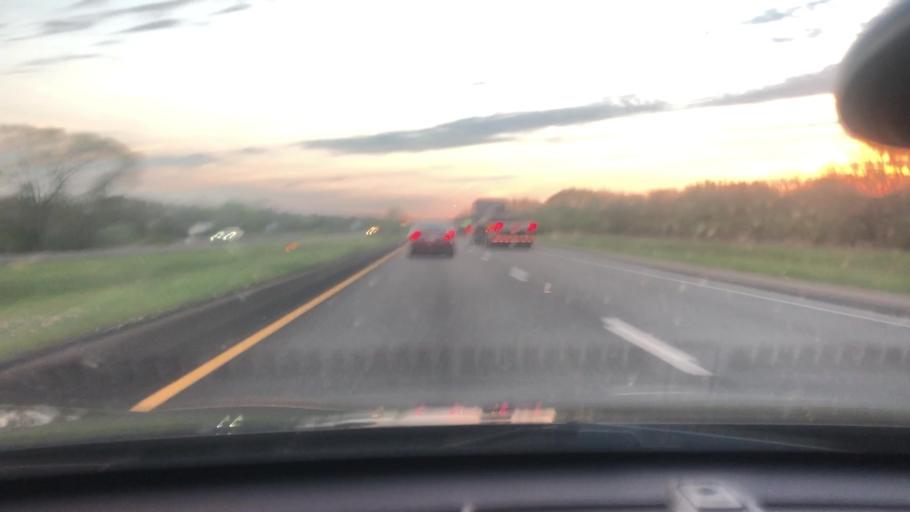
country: US
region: Texas
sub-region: Victoria County
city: Inez
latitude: 28.9147
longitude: -96.7711
